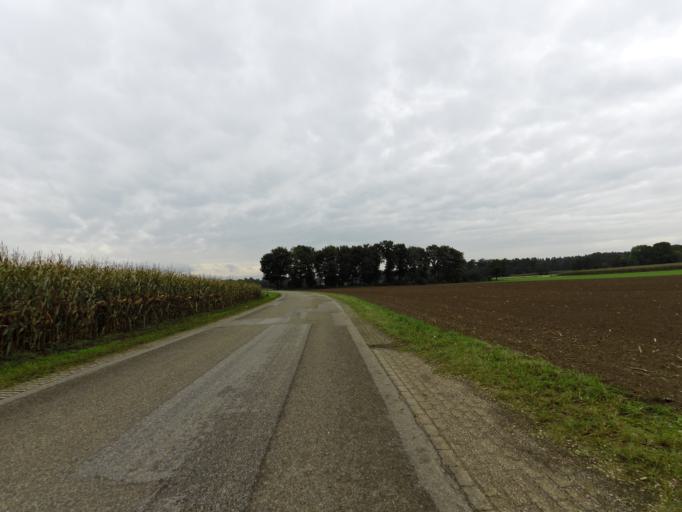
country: NL
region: Gelderland
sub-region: Oude IJsselstreek
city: Gendringen
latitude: 51.8750
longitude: 6.4112
